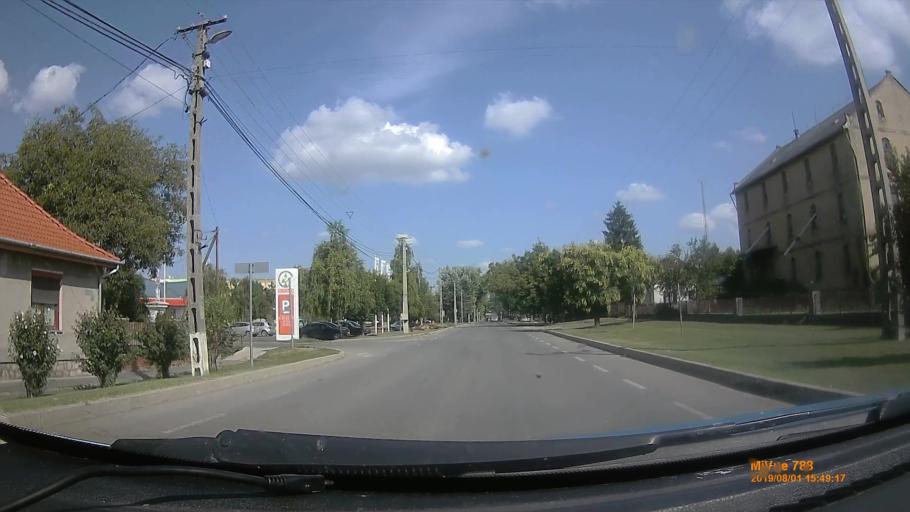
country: HU
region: Baranya
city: Szentlorinc
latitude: 46.0397
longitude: 17.9889
